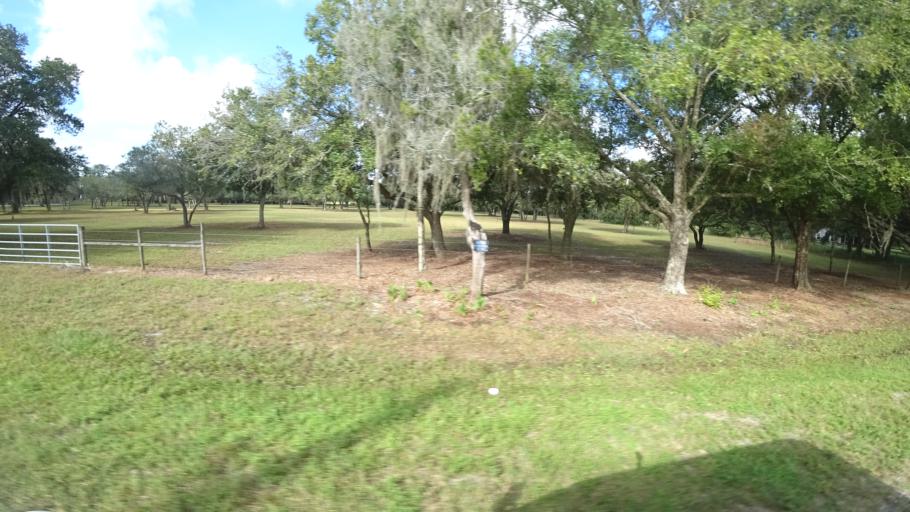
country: US
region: Florida
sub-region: Sarasota County
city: Lake Sarasota
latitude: 27.3847
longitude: -82.2683
